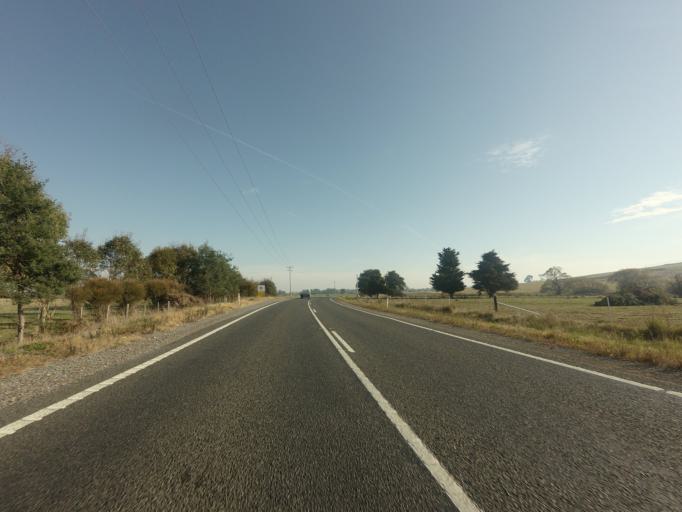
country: AU
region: Tasmania
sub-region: Northern Midlands
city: Longford
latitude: -41.5594
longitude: 147.0674
